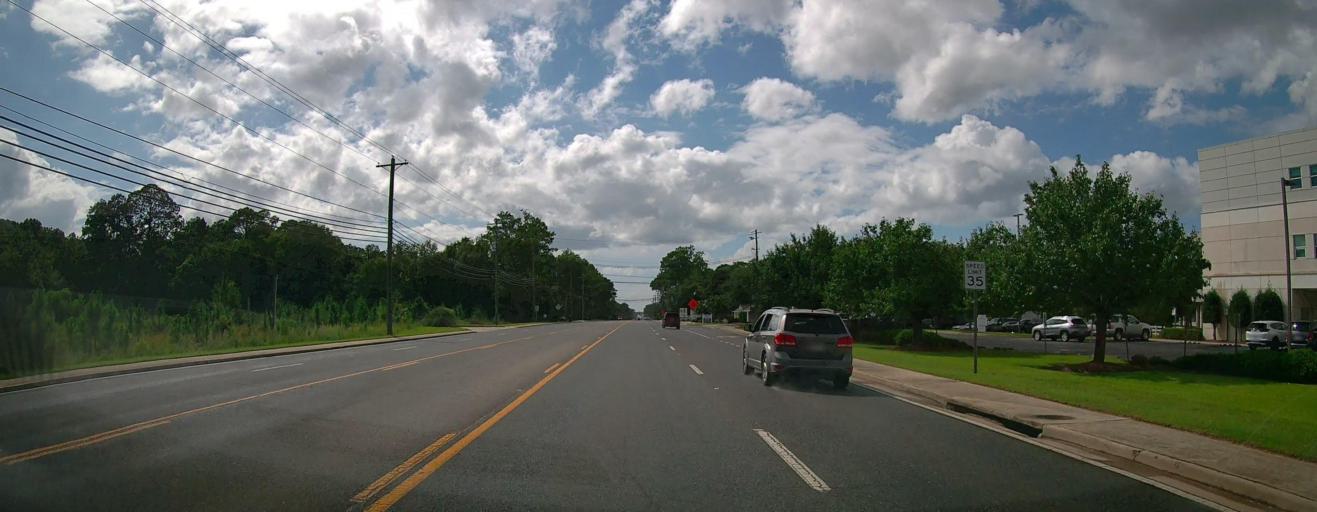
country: US
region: Georgia
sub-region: Coffee County
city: Douglas
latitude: 31.5101
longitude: -82.8646
